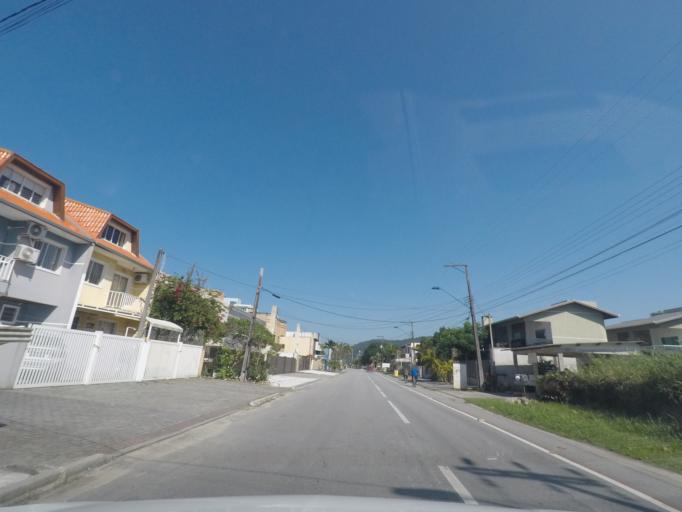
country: BR
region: Parana
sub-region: Guaratuba
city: Guaratuba
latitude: -25.8284
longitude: -48.5382
